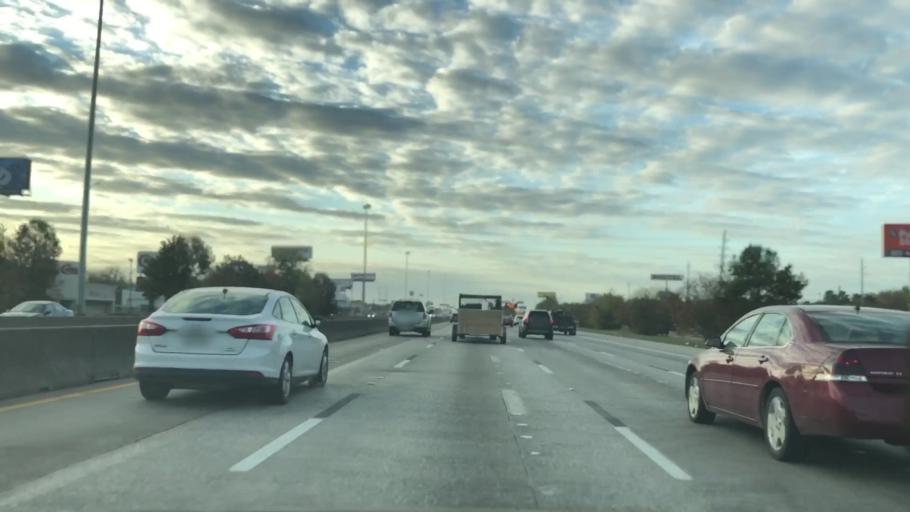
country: US
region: Texas
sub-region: Harris County
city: Aldine
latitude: 29.9064
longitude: -95.4125
